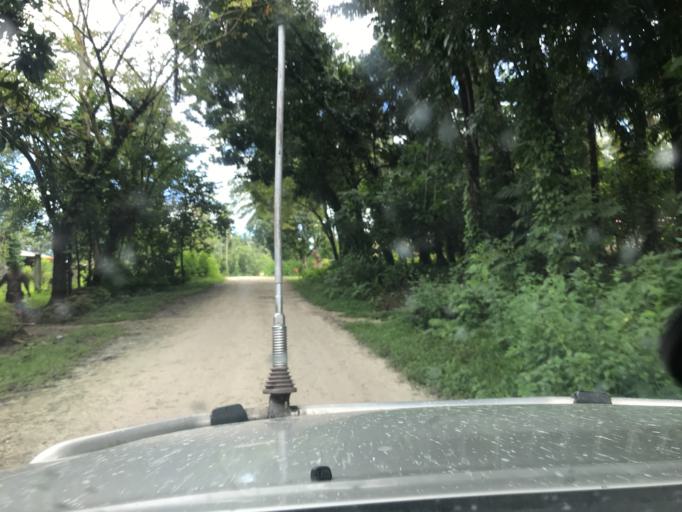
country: SB
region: Malaita
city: Auki
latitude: -8.4048
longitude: 160.5947
